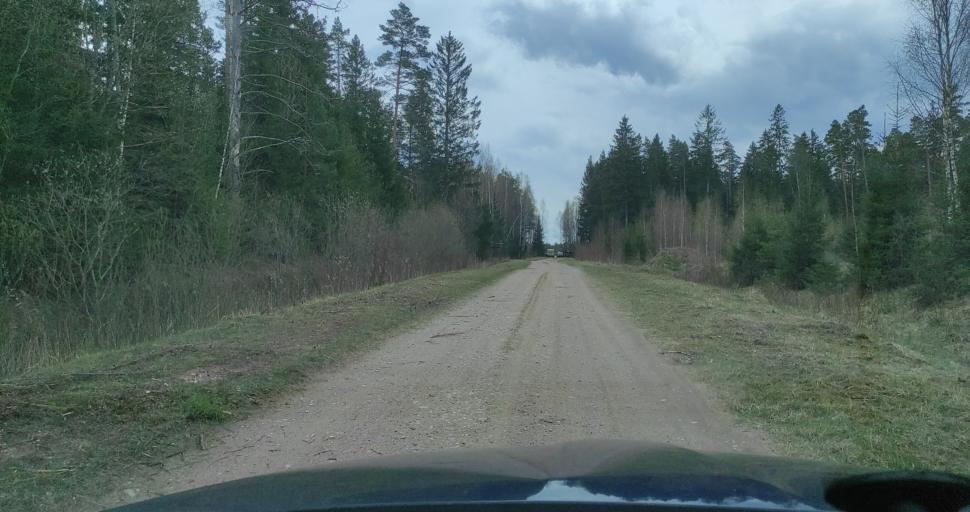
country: LV
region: Dundaga
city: Dundaga
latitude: 57.3588
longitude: 22.1524
